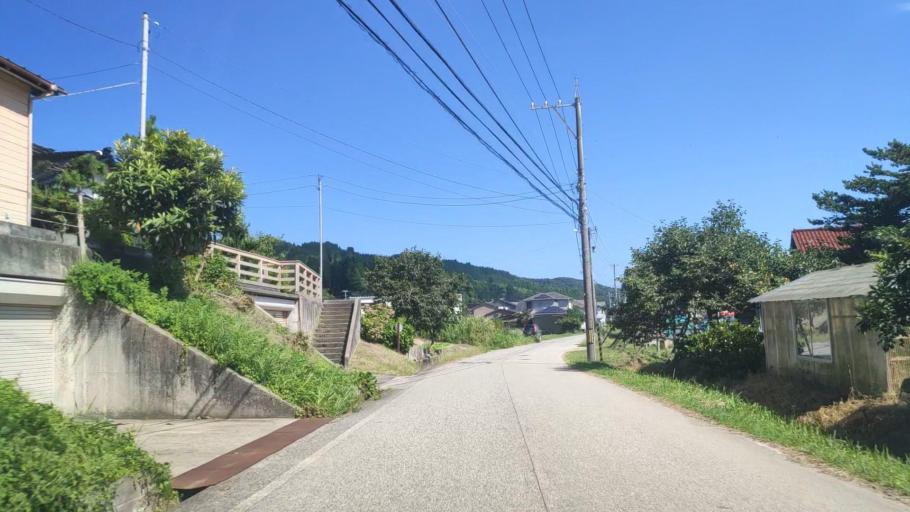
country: JP
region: Ishikawa
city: Nanao
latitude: 37.3735
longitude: 136.8747
